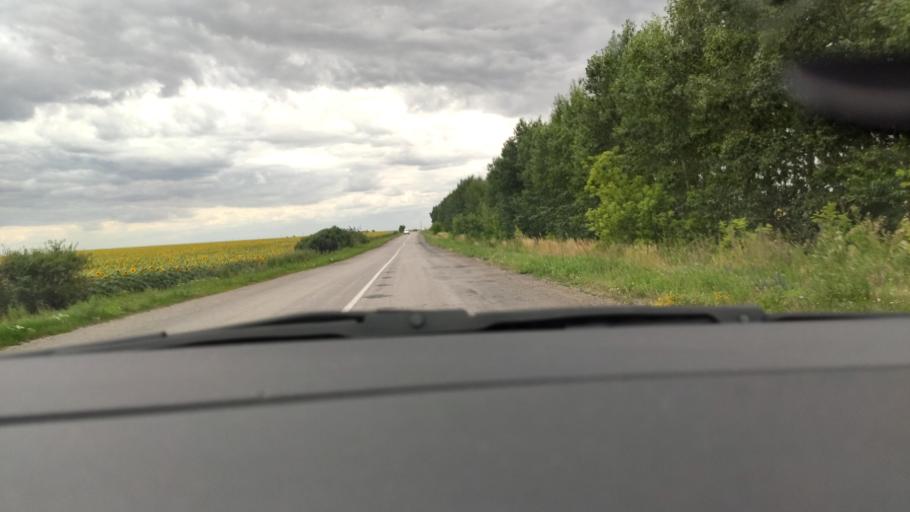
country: RU
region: Voronezj
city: Zemlyansk
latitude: 51.9367
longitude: 38.9769
